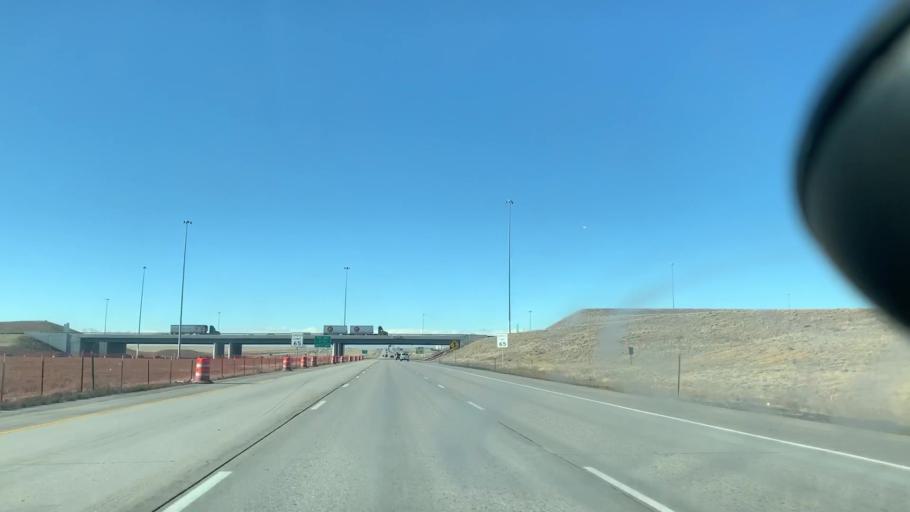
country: US
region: Colorado
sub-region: Adams County
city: Aurora
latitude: 39.8346
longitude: -104.7436
